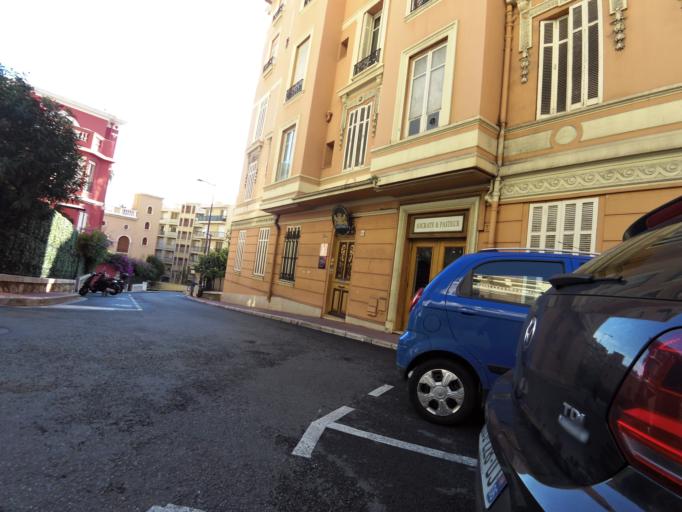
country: MC
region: Commune de Monaco
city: La Condamine
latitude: 43.7378
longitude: 7.4220
